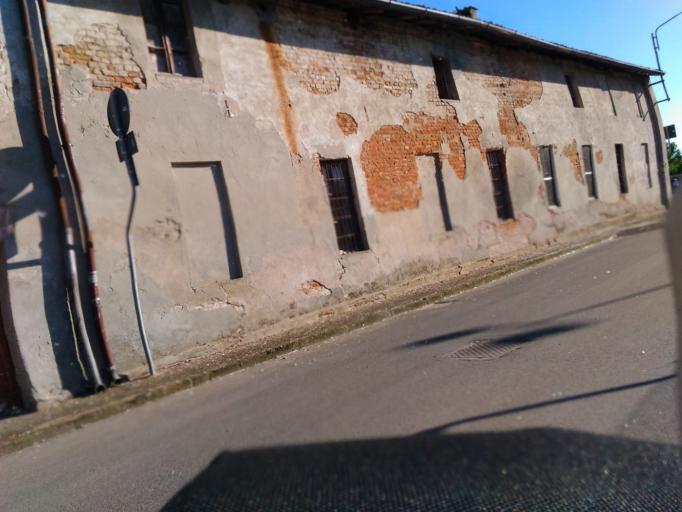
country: IT
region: Lombardy
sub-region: Provincia di Pavia
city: Bascape
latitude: 45.3068
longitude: 9.3149
